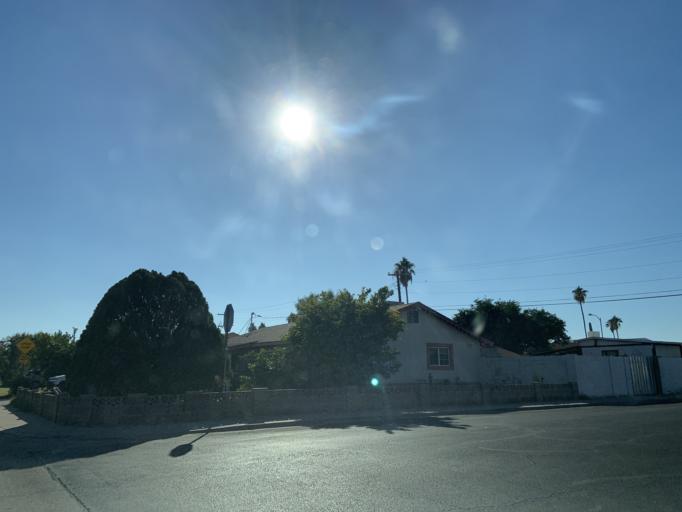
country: US
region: Arizona
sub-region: Maricopa County
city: Tempe
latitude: 33.4030
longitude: -111.8698
